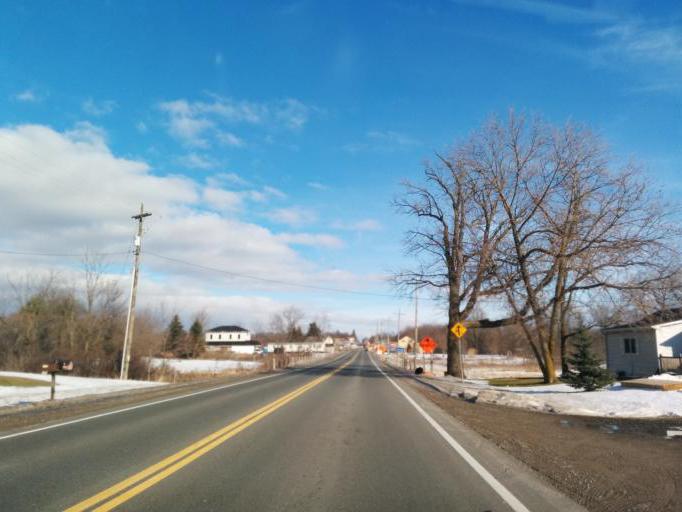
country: CA
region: Ontario
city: Ancaster
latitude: 42.9474
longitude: -79.8675
